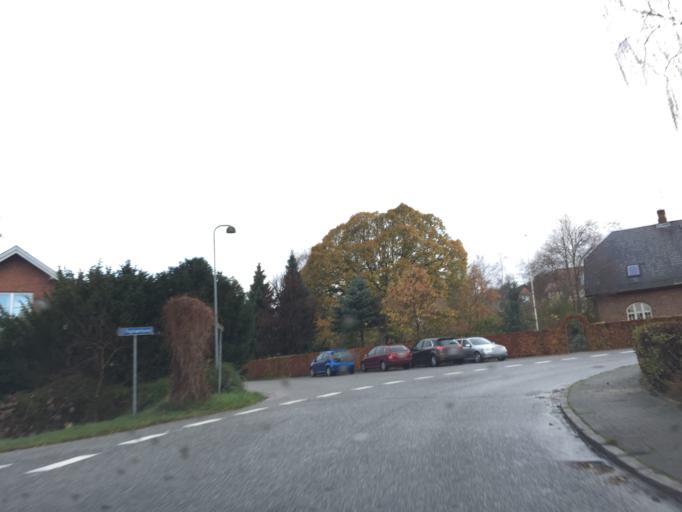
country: DK
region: Central Jutland
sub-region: Favrskov Kommune
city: Hammel
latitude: 56.2286
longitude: 9.7354
